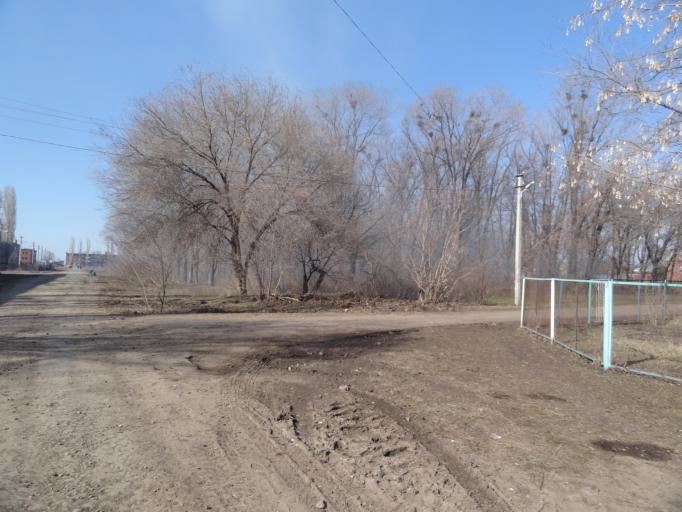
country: RU
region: Saratov
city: Engel's
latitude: 51.4302
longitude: 46.1826
